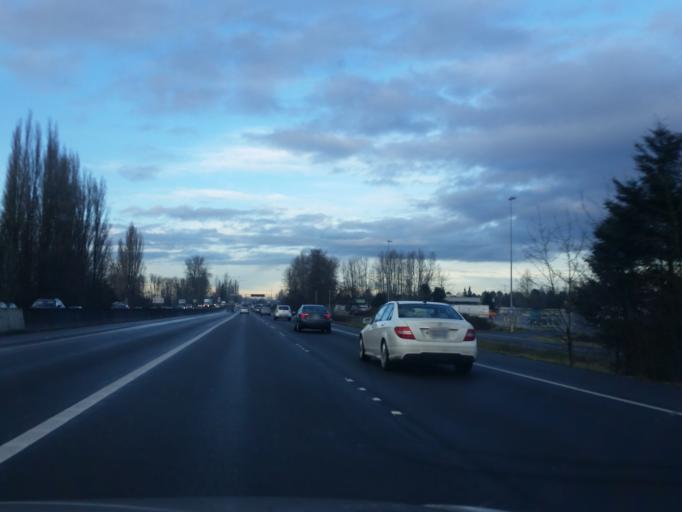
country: US
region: Washington
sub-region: King County
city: Kent
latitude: 47.3644
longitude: -122.2445
